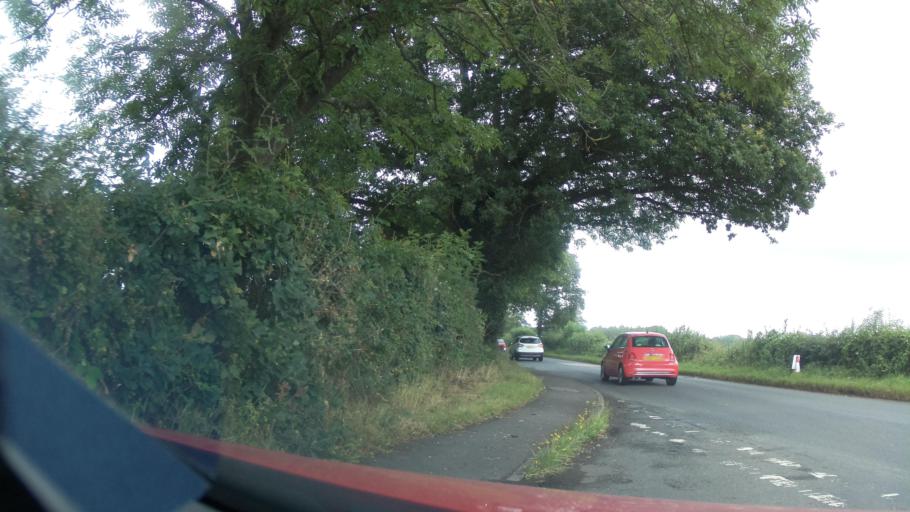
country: GB
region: England
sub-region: Solihull
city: Cheswick Green
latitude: 52.3824
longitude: -1.8222
